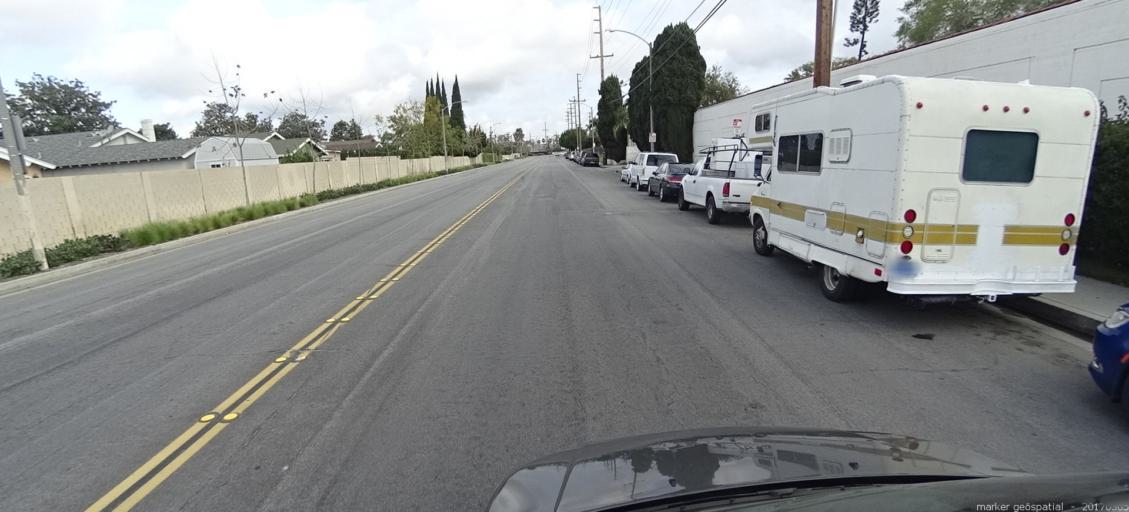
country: US
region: California
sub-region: Orange County
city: Orange
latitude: 33.7933
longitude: -117.8976
